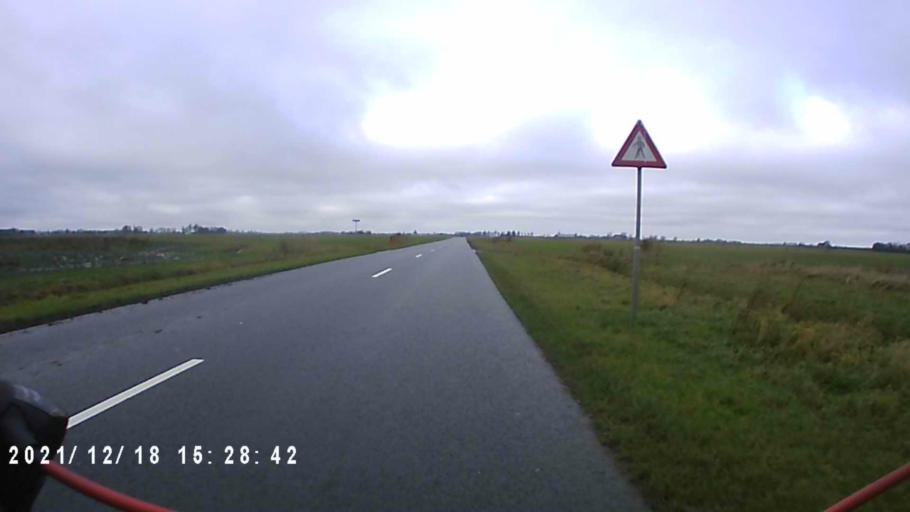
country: NL
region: Friesland
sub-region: Gemeente Dongeradeel
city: Anjum
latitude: 53.3326
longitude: 6.1436
